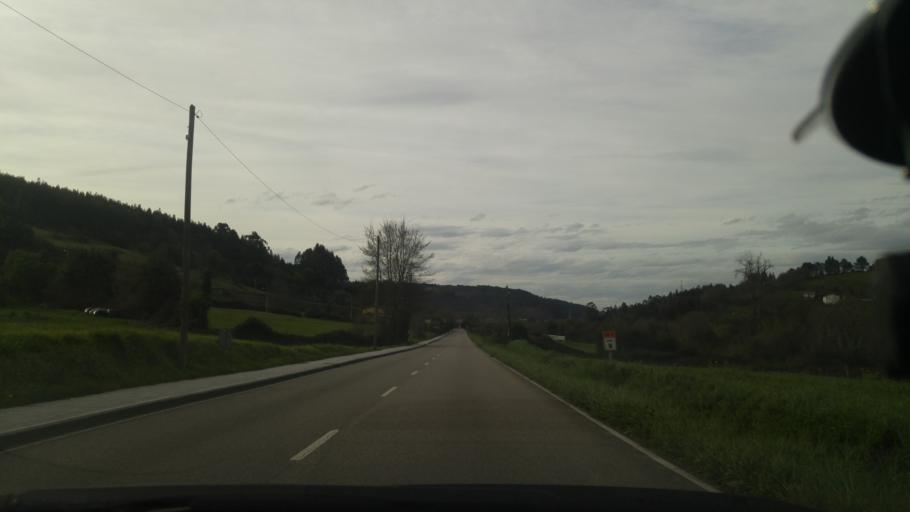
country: ES
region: Asturias
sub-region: Province of Asturias
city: Corvera de Asturias
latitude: 43.4991
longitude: -5.8589
